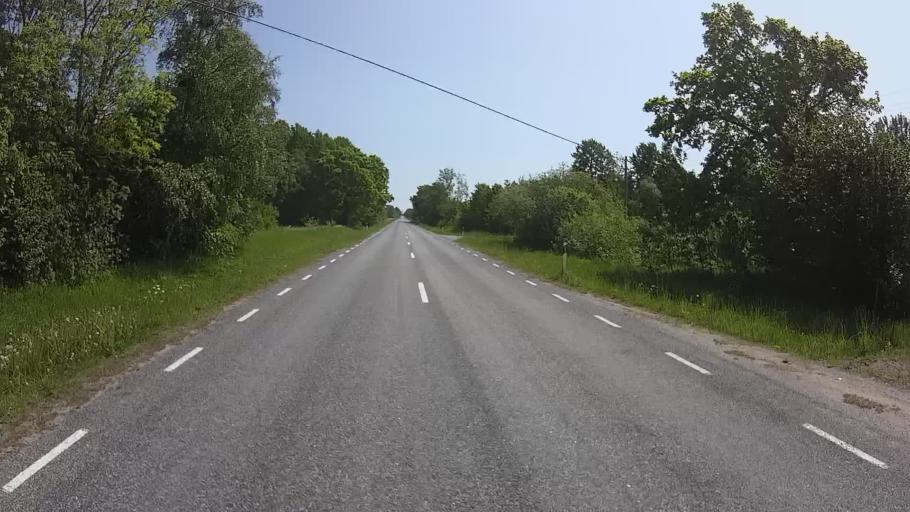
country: EE
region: Saare
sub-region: Kuressaare linn
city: Kuressaare
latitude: 58.3732
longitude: 22.0425
